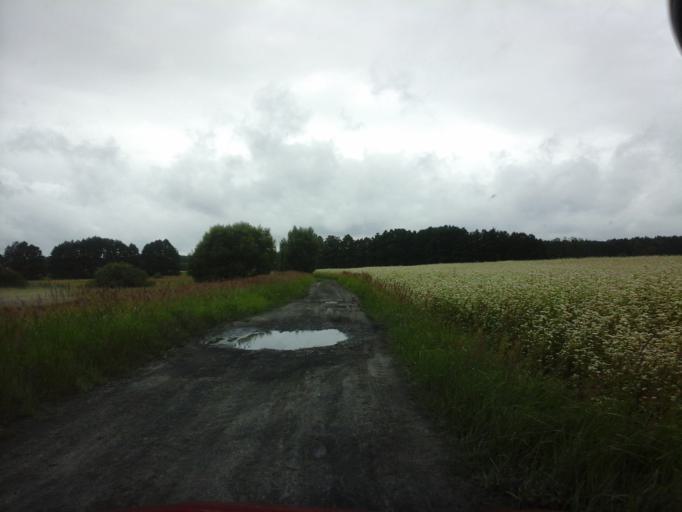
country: PL
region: West Pomeranian Voivodeship
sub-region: Powiat choszczenski
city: Bierzwnik
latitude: 53.0593
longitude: 15.7181
